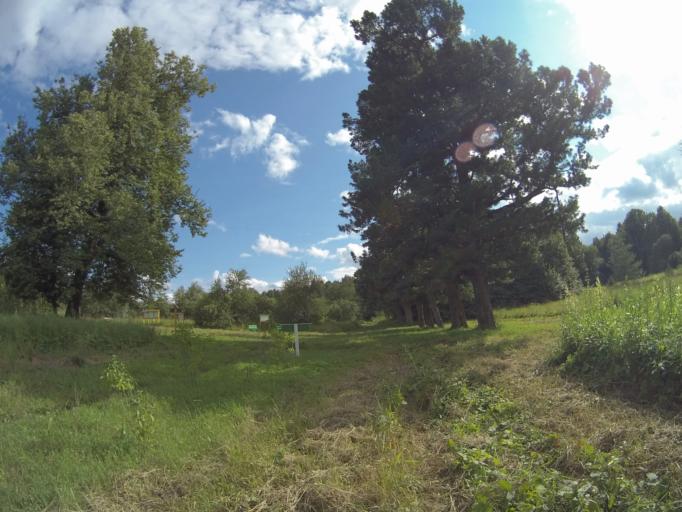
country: RU
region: Vladimir
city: Suzdal'
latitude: 56.2972
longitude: 40.3602
